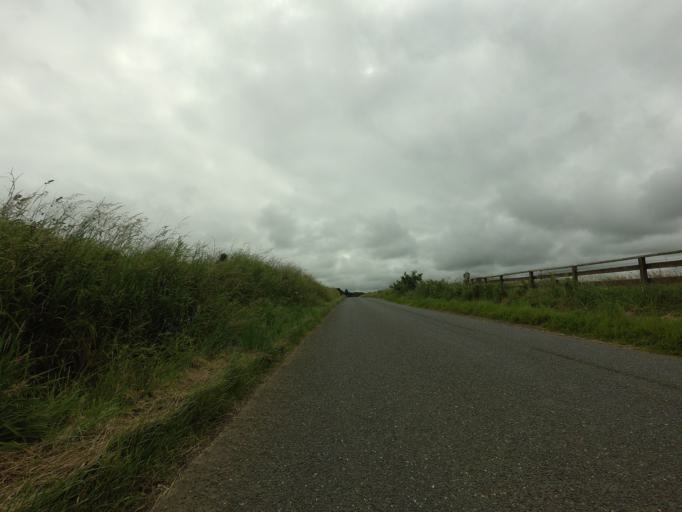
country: GB
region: Scotland
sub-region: Aberdeenshire
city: Turriff
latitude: 57.5345
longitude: -2.4257
